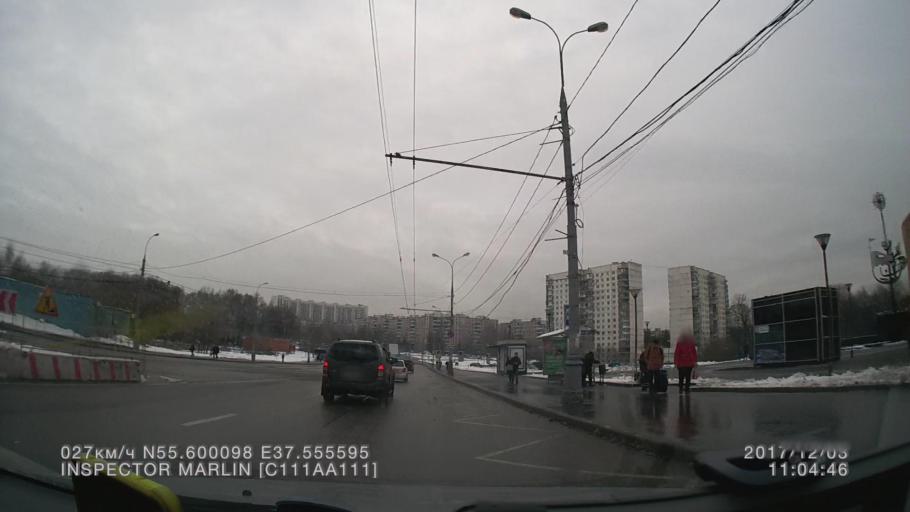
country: RU
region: Moscow
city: Yasenevo
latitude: 55.6002
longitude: 37.5555
